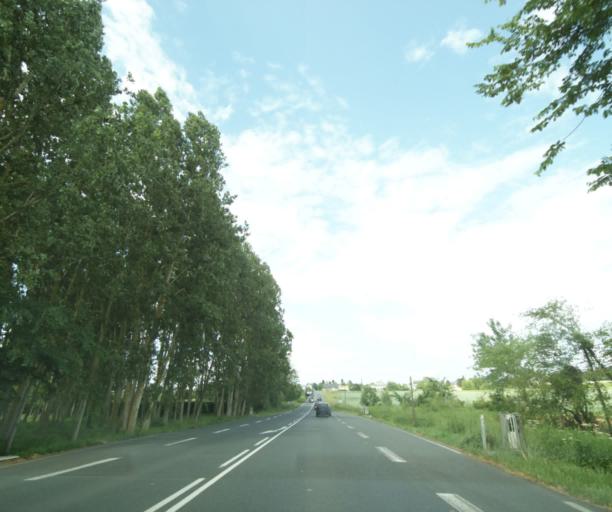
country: FR
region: Pays de la Loire
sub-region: Departement de Maine-et-Loire
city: Distre
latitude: 47.1907
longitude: -0.1280
